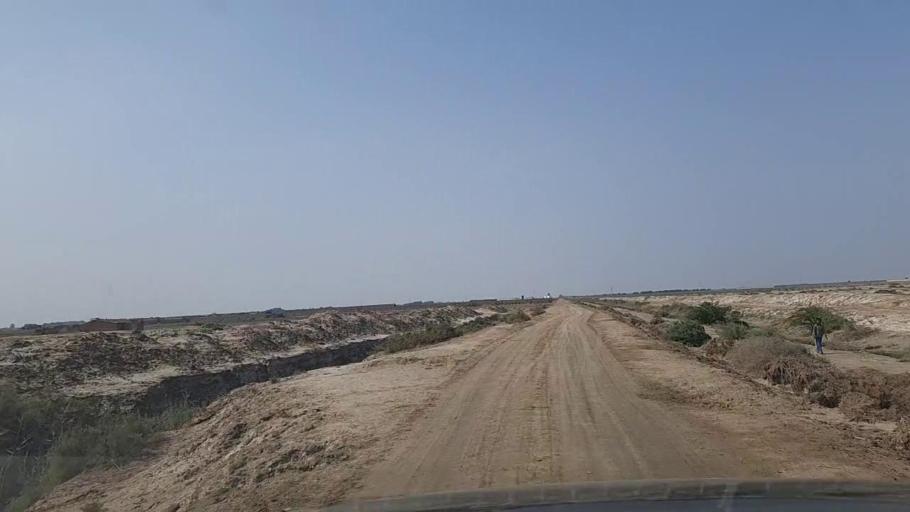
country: PK
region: Sindh
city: Gharo
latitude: 24.7046
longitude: 67.5711
